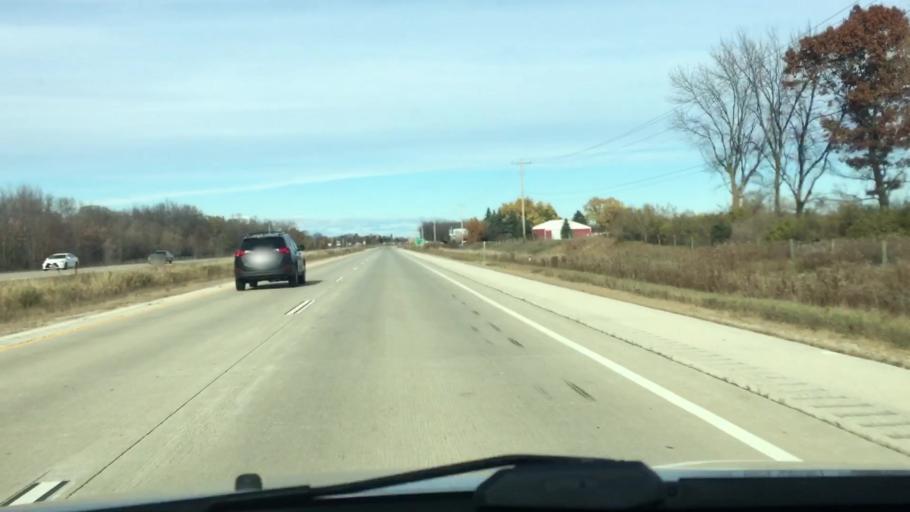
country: US
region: Wisconsin
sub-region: Brown County
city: Bellevue
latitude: 44.5639
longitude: -87.8796
